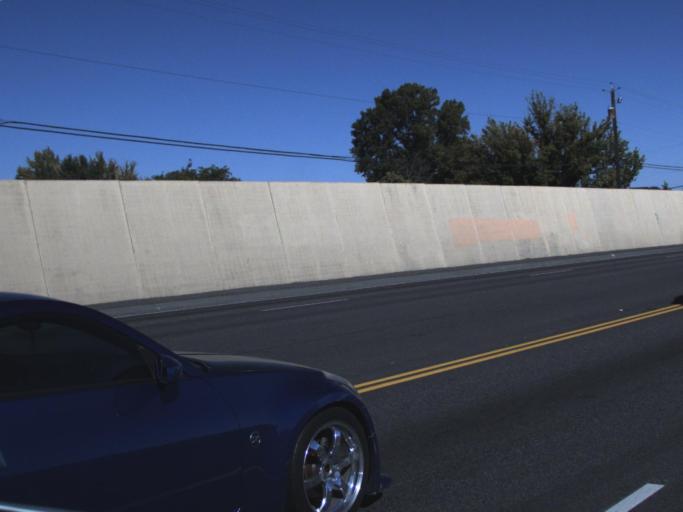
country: US
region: Washington
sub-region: Benton County
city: Kennewick
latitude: 46.2150
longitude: -119.1487
